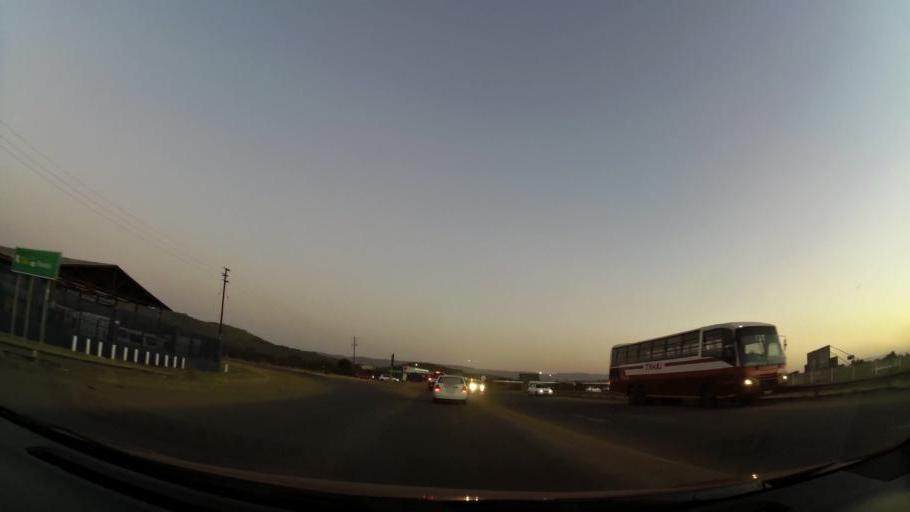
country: ZA
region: North-West
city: Ga-Rankuwa
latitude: -25.6229
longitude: 27.9626
